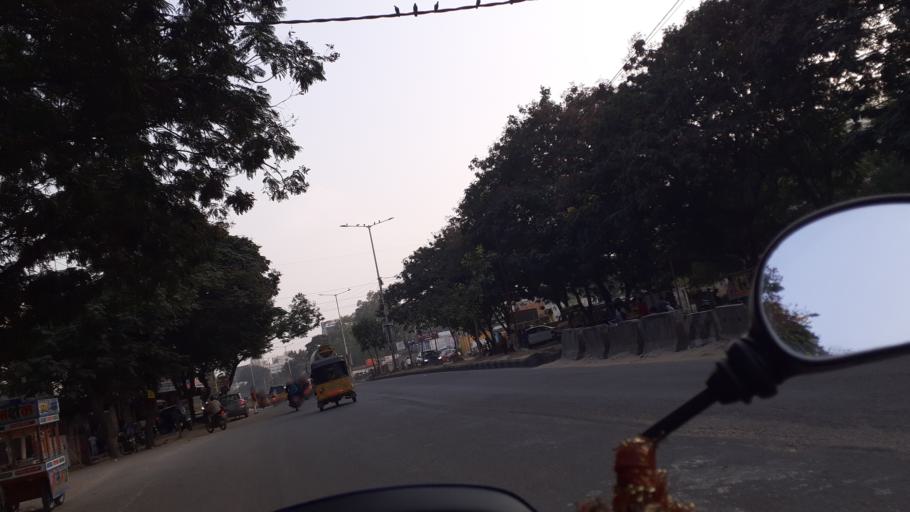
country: IN
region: Telangana
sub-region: Rangareddi
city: Kukatpalli
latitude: 17.4718
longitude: 78.3649
